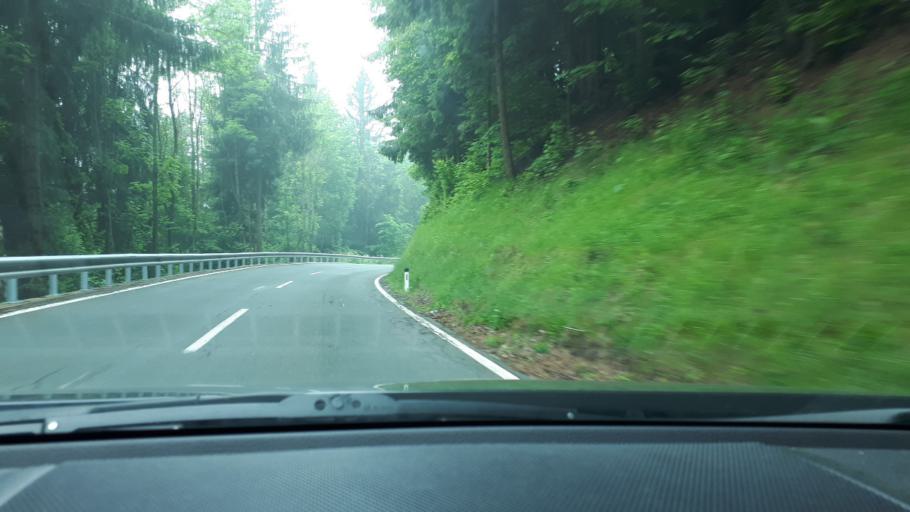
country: AT
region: Carinthia
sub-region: Politischer Bezirk Wolfsberg
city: Preitenegg
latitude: 46.9368
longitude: 14.9045
